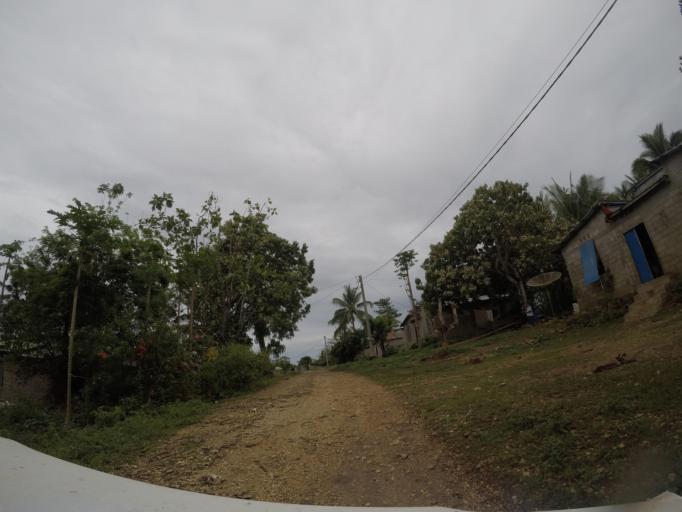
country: TL
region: Lautem
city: Lospalos
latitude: -8.5327
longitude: 127.0001
